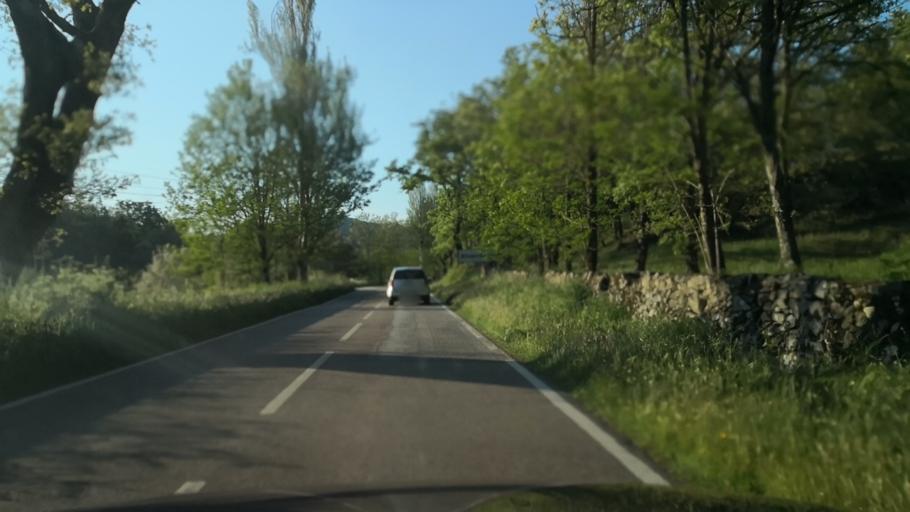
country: PT
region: Portalegre
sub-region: Marvao
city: Marvao
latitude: 39.3539
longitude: -7.4064
